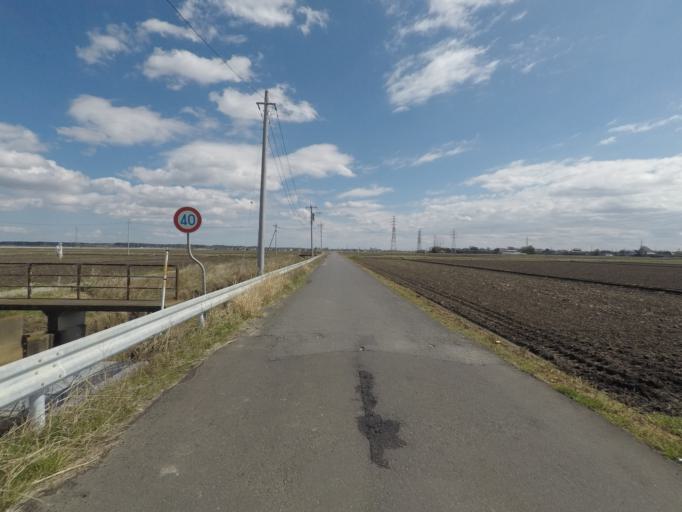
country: JP
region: Ibaraki
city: Fujishiro
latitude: 35.9413
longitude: 140.1058
